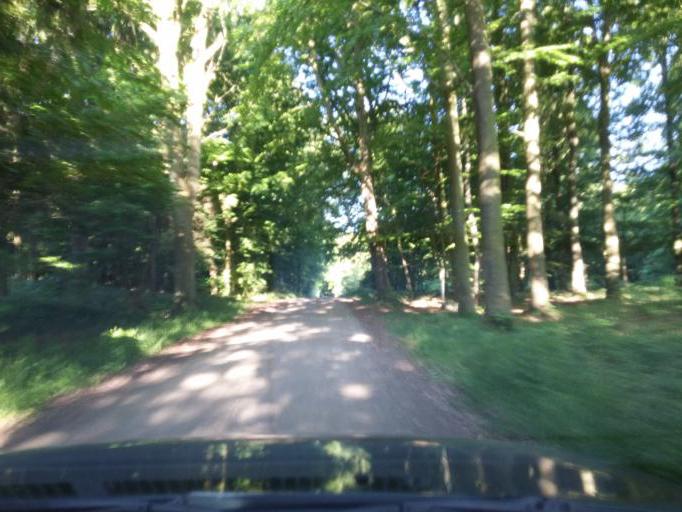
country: DK
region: South Denmark
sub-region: Aabenraa Kommune
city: Lojt Kirkeby
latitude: 55.1298
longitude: 9.5116
